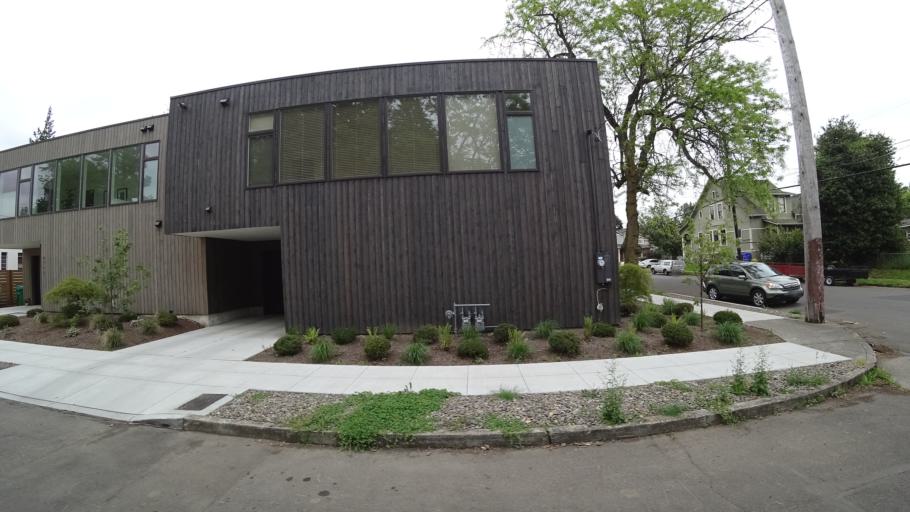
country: US
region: Oregon
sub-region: Multnomah County
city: Portland
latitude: 45.5569
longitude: -122.6719
